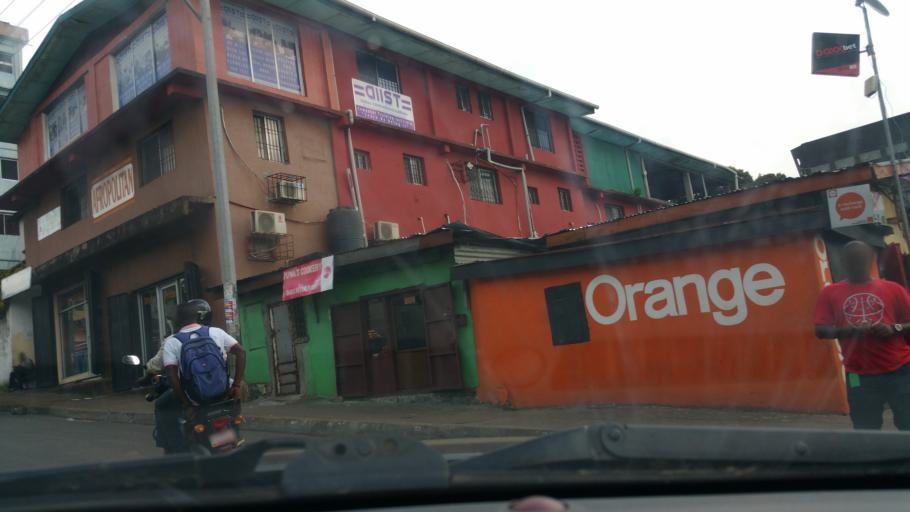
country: LR
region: Montserrado
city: Monrovia
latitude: 6.3163
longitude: -10.8095
